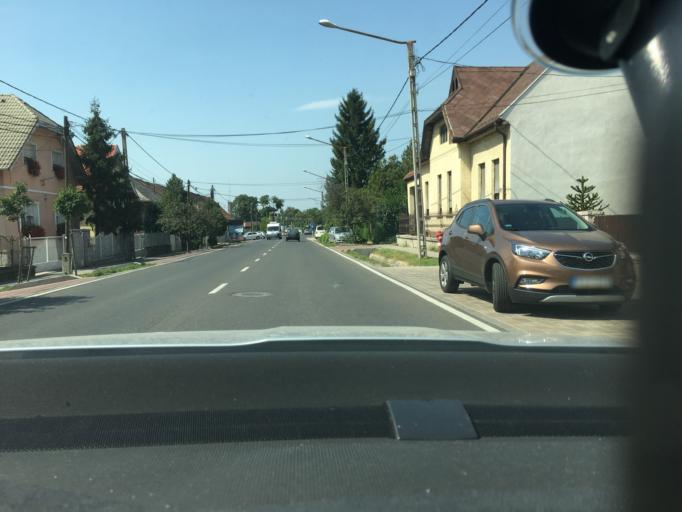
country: HU
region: Pest
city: Csomor
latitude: 47.5194
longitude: 19.2224
